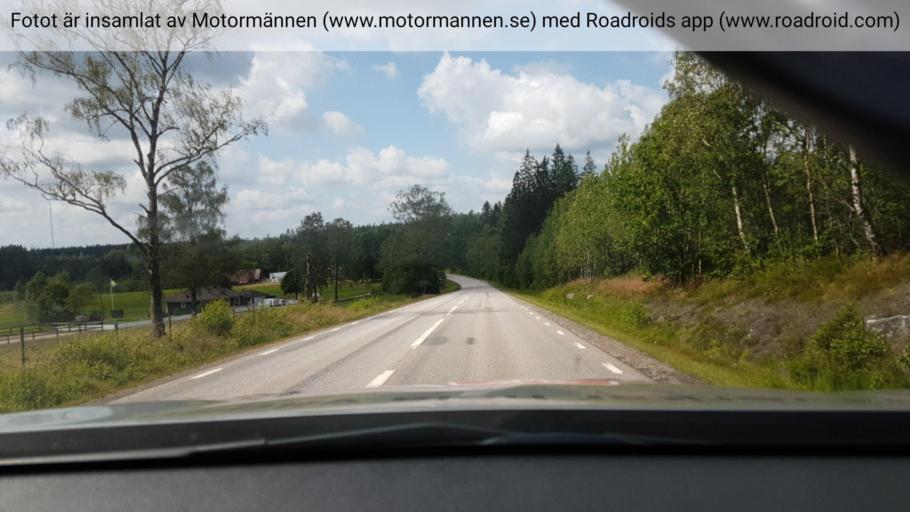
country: SE
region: Vaestra Goetaland
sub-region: Svenljunga Kommun
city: Svenljunga
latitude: 57.4864
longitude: 13.0019
